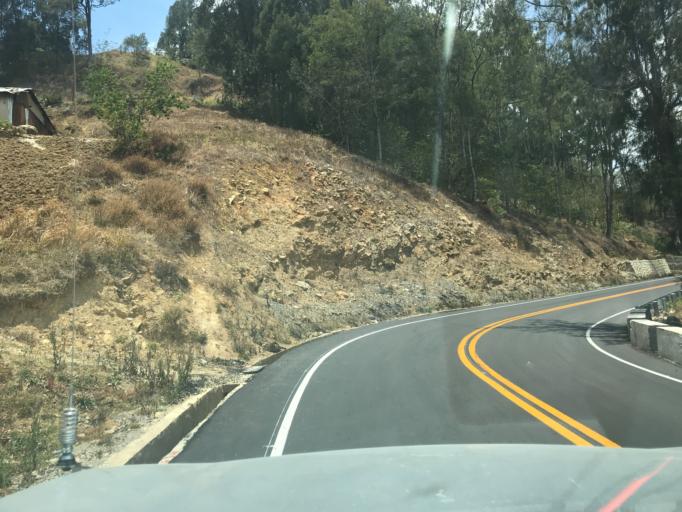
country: TL
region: Manufahi
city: Same
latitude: -8.8762
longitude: 125.5903
